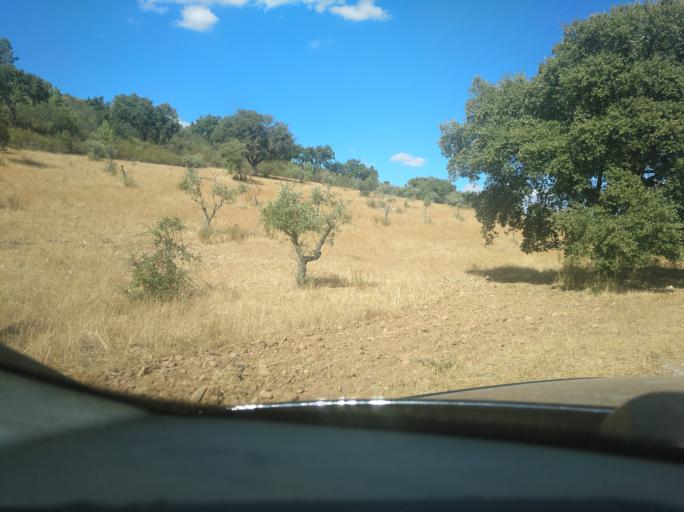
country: ES
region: Extremadura
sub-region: Provincia de Badajoz
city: La Codosera
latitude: 39.1481
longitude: -7.1723
